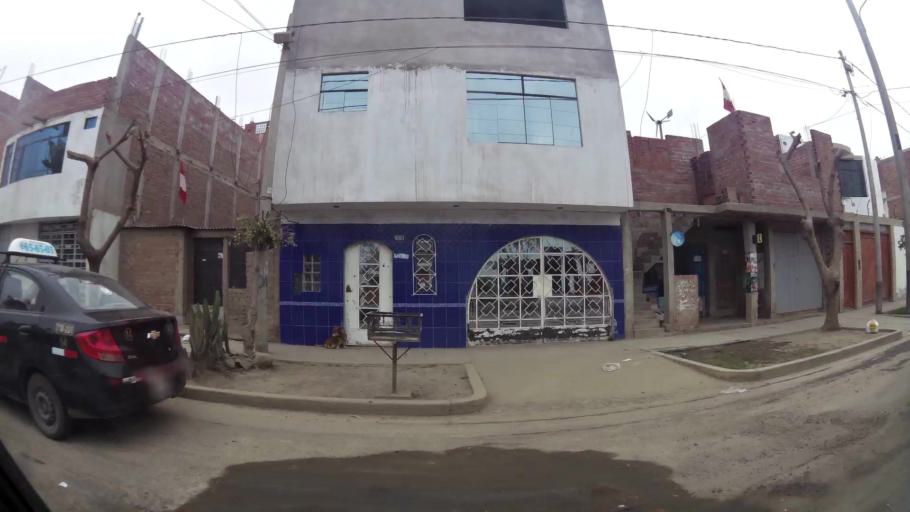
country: PE
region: La Libertad
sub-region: Provincia de Trujillo
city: Buenos Aires
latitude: -8.1225
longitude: -79.0463
